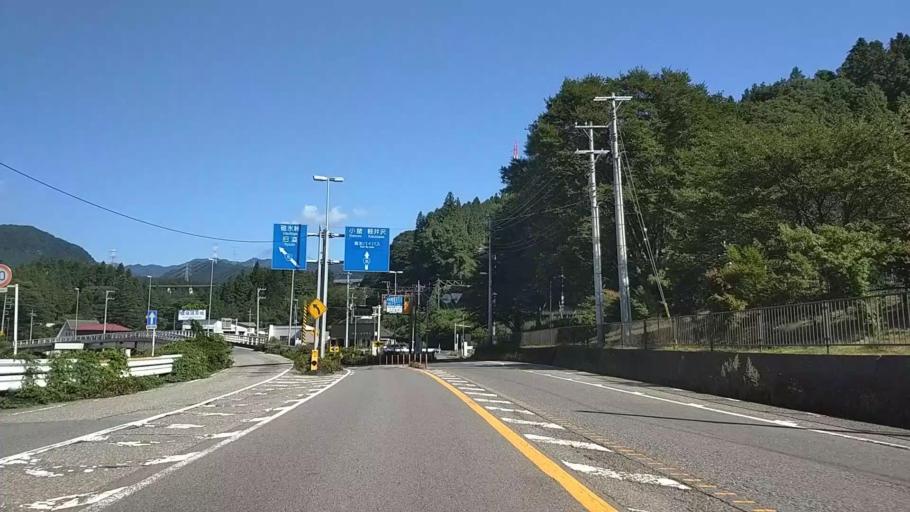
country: JP
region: Gunma
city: Annaka
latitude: 36.3374
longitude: 138.7311
